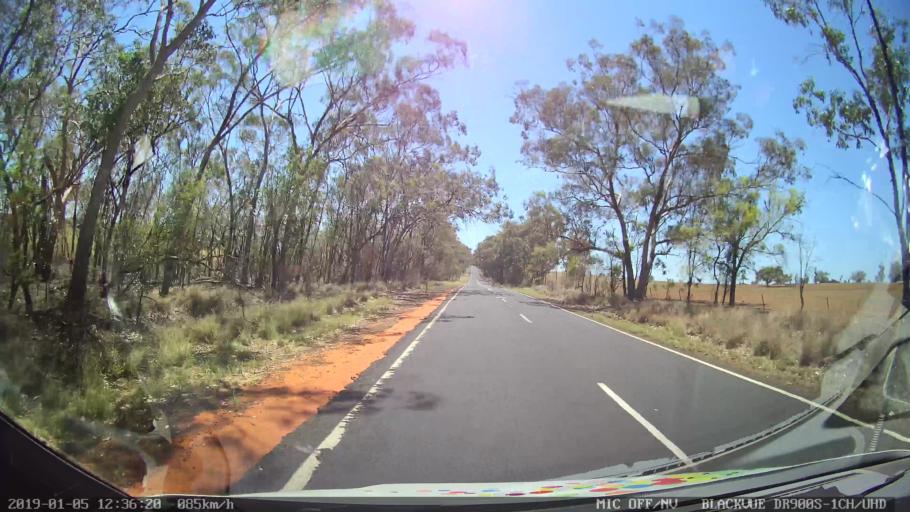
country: AU
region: New South Wales
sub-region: Warrumbungle Shire
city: Coonabarabran
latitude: -31.2075
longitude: 149.4387
